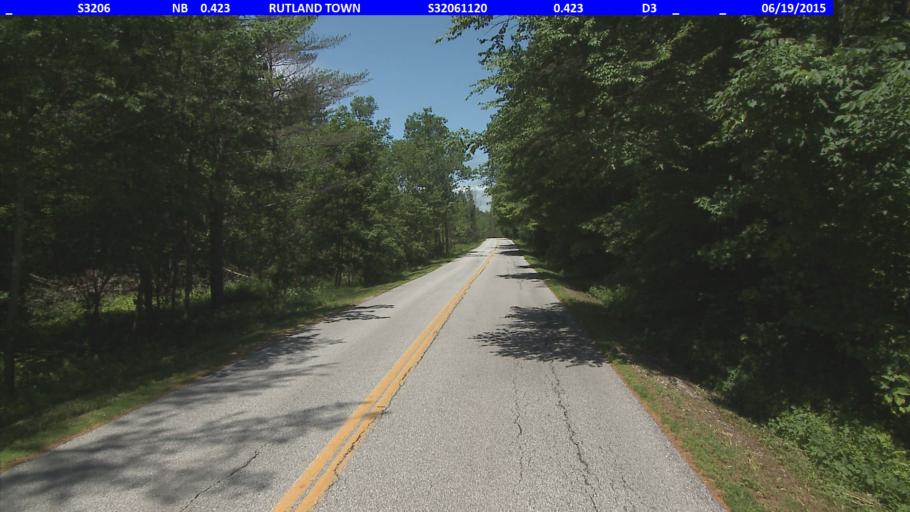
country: US
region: Vermont
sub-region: Rutland County
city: Rutland
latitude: 43.6357
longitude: -72.9902
